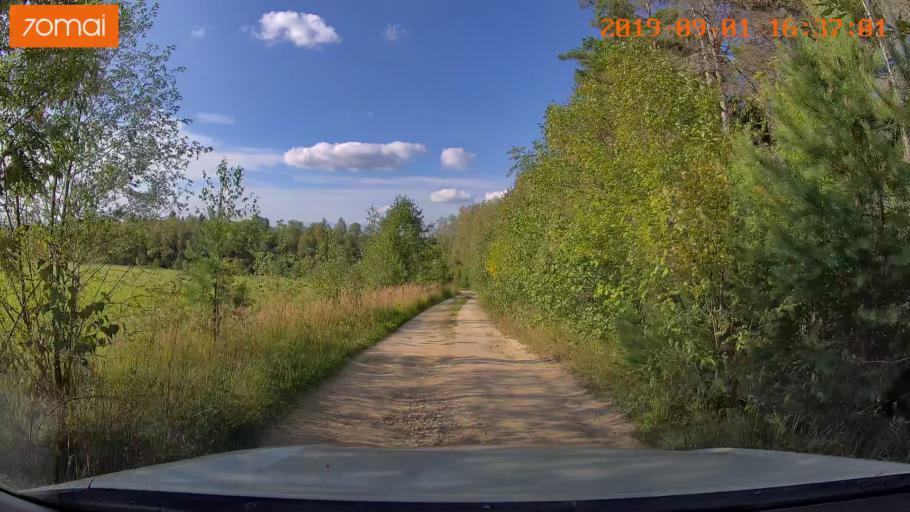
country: RU
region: Kaluga
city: Maloyaroslavets
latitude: 54.9487
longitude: 36.4750
